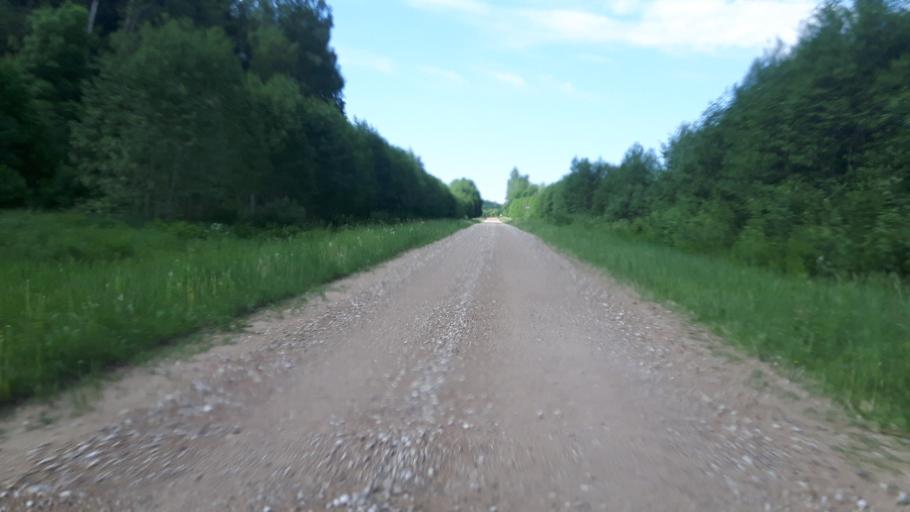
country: EE
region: Paernumaa
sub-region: Vaendra vald (alev)
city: Vandra
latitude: 58.7063
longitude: 25.0349
